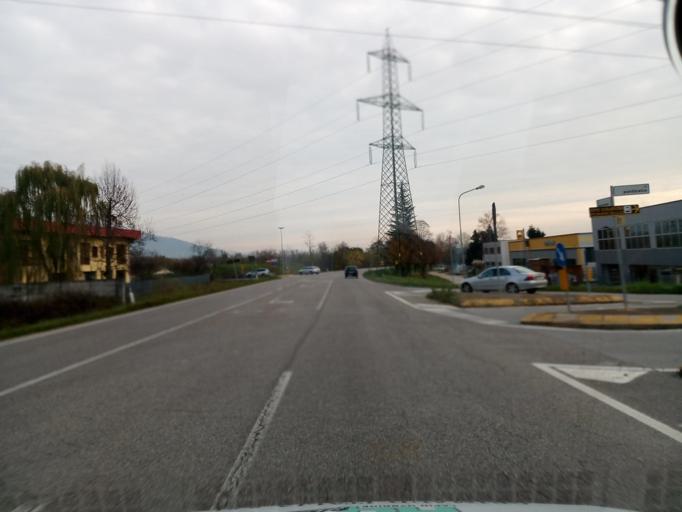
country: IT
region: Veneto
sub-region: Provincia di Treviso
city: Caniezza
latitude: 45.8533
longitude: 11.8984
